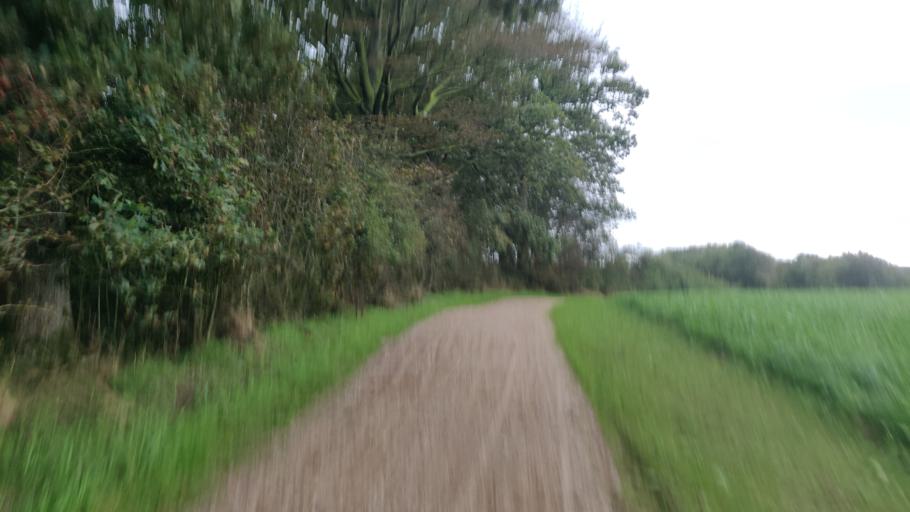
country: DK
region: South Denmark
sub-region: Kolding Kommune
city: Lunderskov
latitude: 55.5417
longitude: 9.3345
